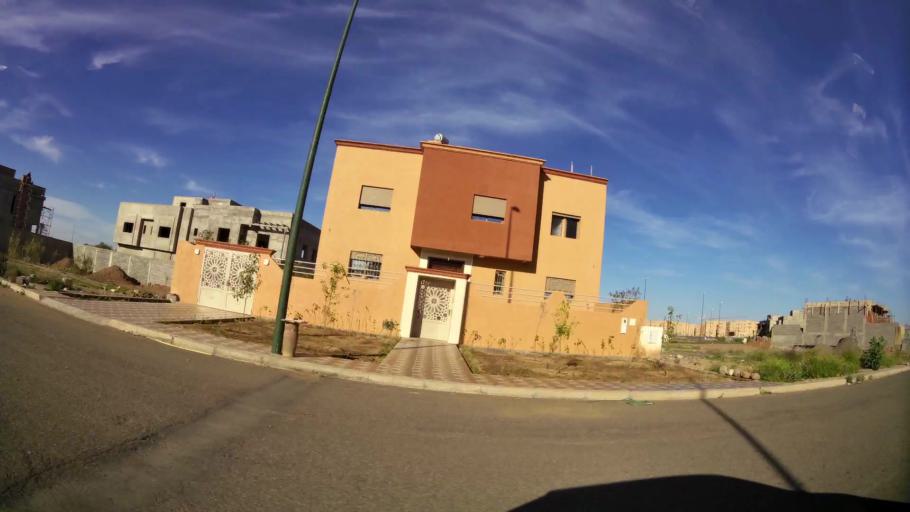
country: MA
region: Marrakech-Tensift-Al Haouz
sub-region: Marrakech
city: Marrakesh
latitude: 31.6728
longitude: -8.0717
